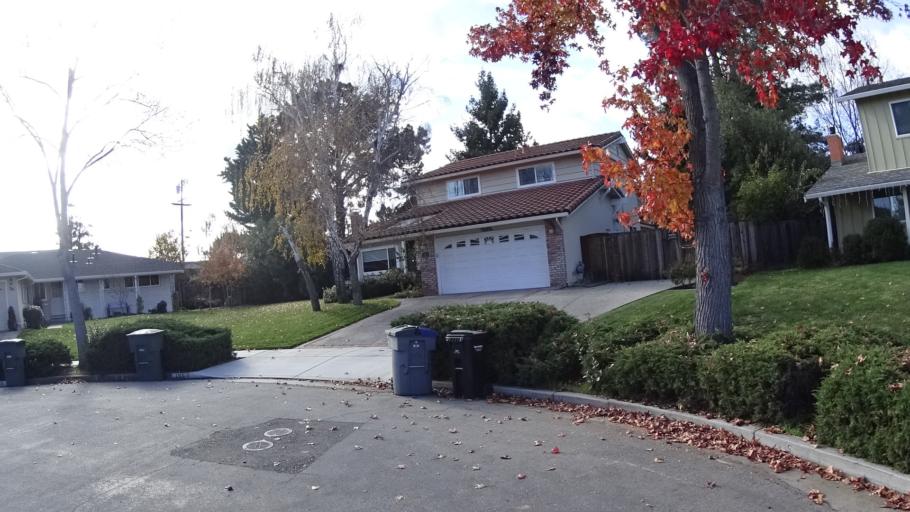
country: US
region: California
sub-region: Santa Clara County
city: Sunnyvale
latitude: 37.3490
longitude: -122.0451
